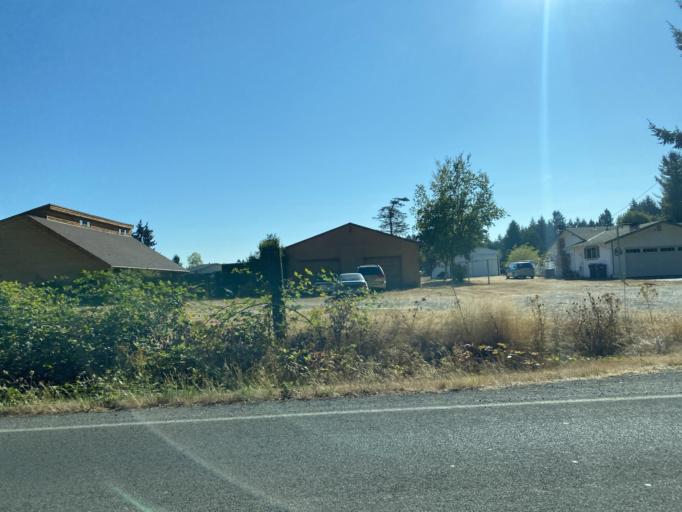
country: US
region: Washington
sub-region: Thurston County
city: Tanglewilde-Thompson Place
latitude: 47.0098
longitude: -122.7386
